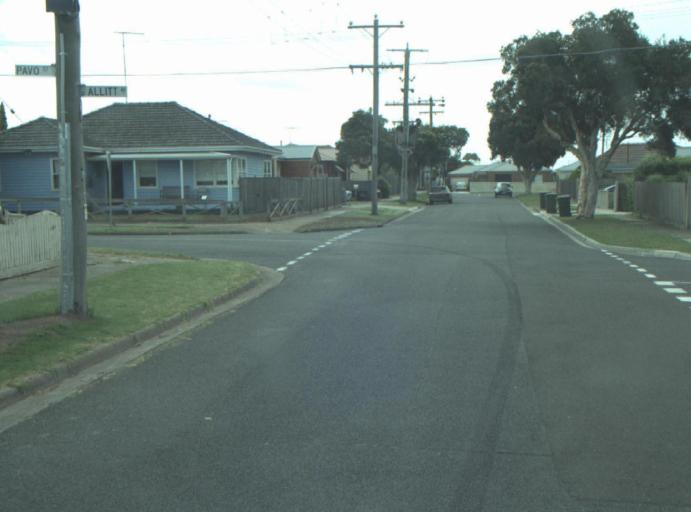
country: AU
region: Victoria
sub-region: Greater Geelong
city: Wandana Heights
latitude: -38.1809
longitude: 144.3331
